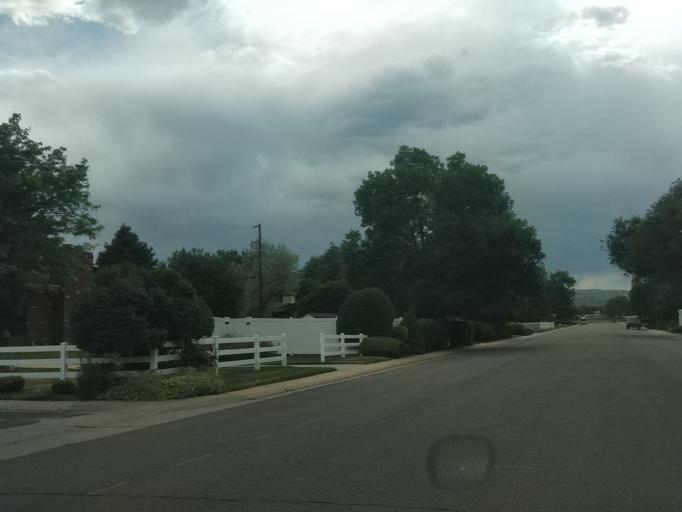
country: US
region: Colorado
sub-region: Jefferson County
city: Lakewood
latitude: 39.7033
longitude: -105.0967
